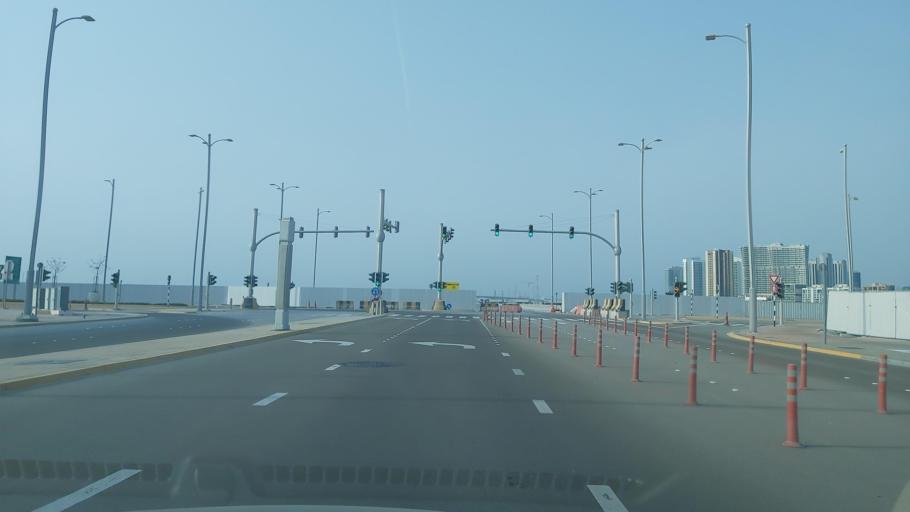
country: AE
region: Abu Dhabi
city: Abu Dhabi
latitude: 24.4975
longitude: 54.3987
